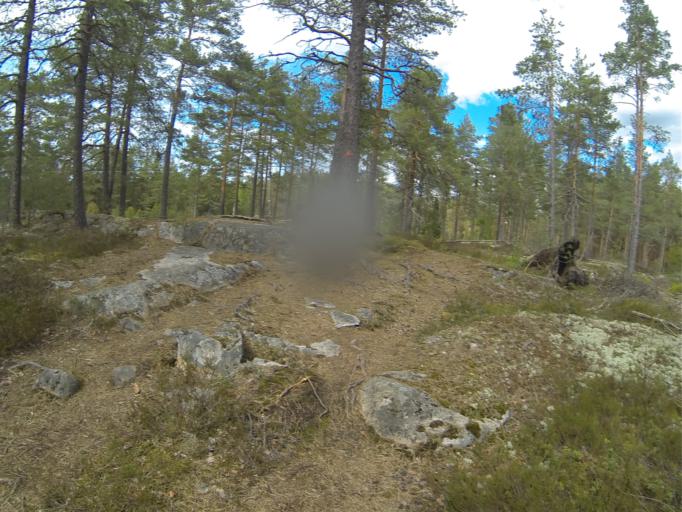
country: FI
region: Varsinais-Suomi
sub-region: Salo
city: Salo
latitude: 60.3513
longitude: 23.1106
